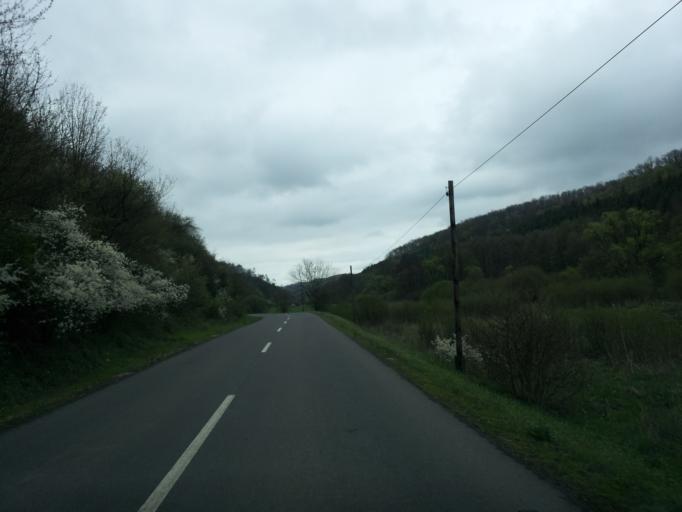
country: HU
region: Borsod-Abauj-Zemplen
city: Rudabanya
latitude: 48.4785
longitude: 20.5738
